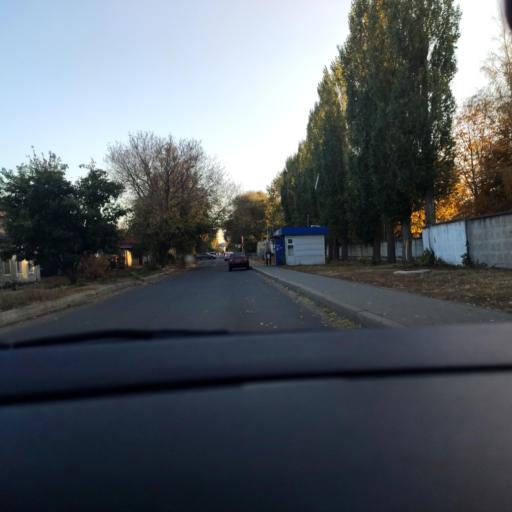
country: RU
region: Voronezj
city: Voronezh
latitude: 51.6941
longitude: 39.2142
